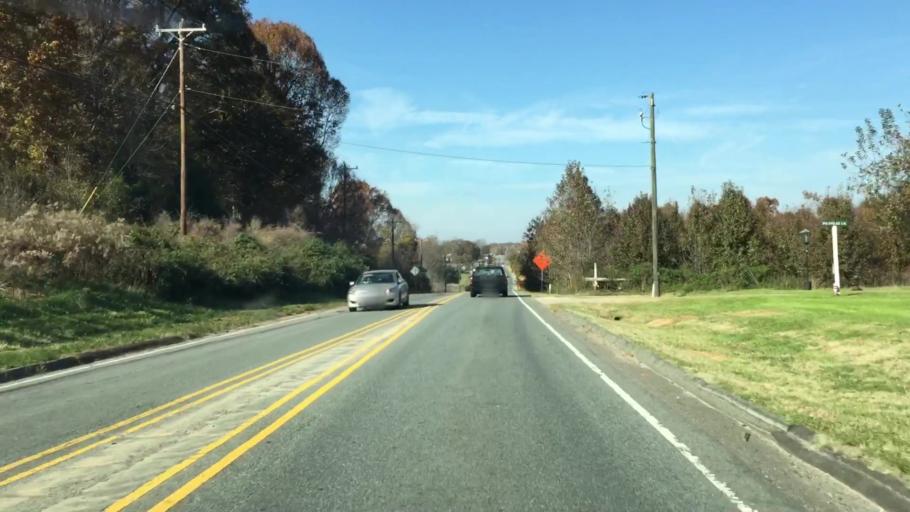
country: US
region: North Carolina
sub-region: Iredell County
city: Troutman
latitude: 35.6603
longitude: -80.8491
